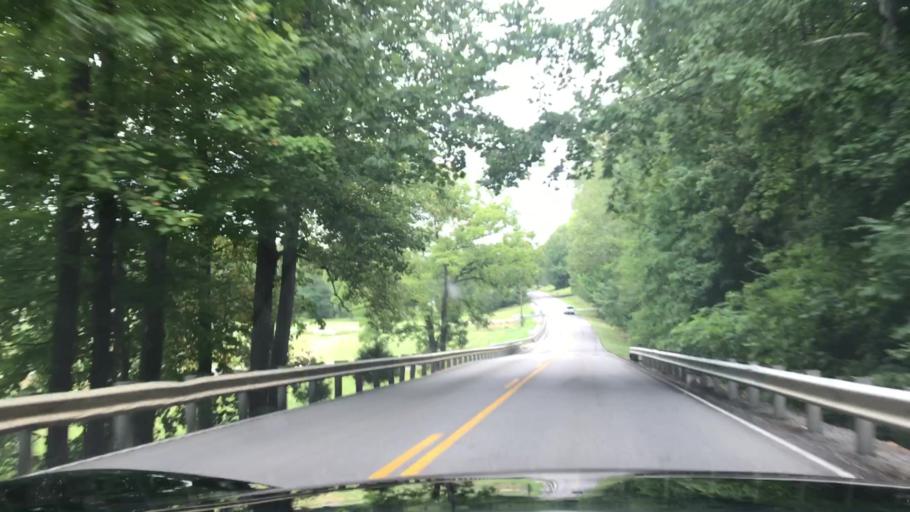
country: US
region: Kentucky
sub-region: Muhlenberg County
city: Central City
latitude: 37.2053
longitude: -87.0772
